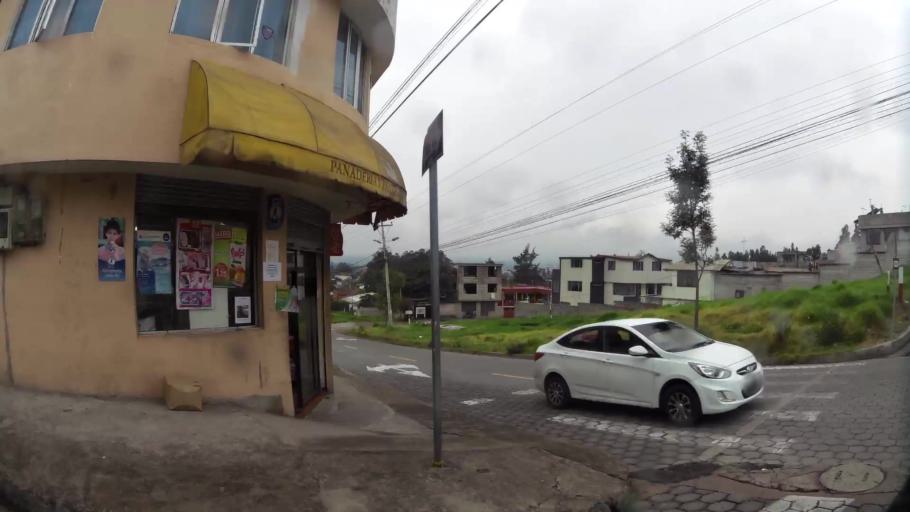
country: EC
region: Pichincha
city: Sangolqui
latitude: -0.2795
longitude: -78.4699
